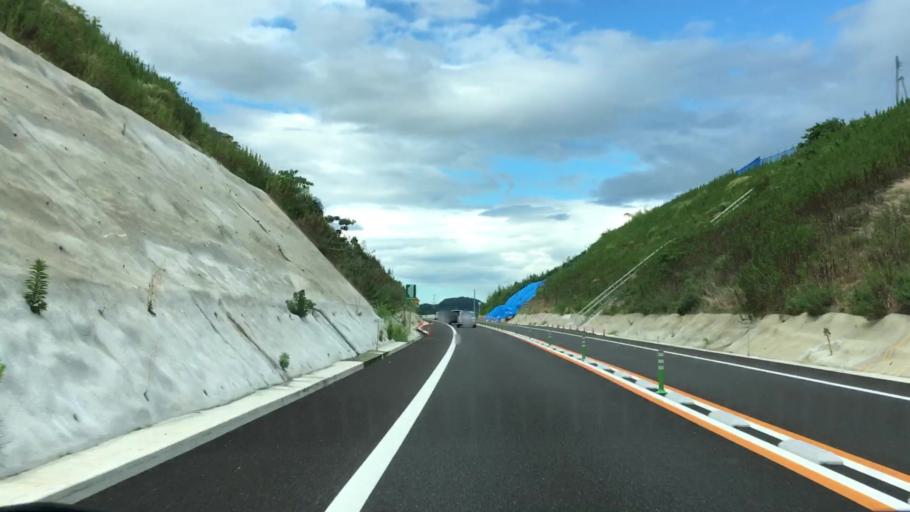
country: JP
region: Saga Prefecture
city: Imaricho-ko
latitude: 33.3215
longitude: 129.9260
